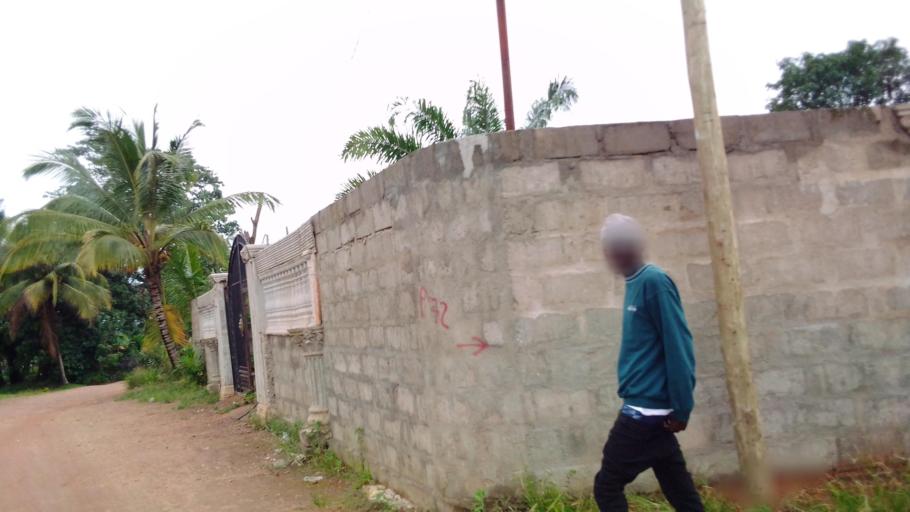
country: SL
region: Eastern Province
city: Kenema
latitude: 7.8548
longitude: -11.1951
